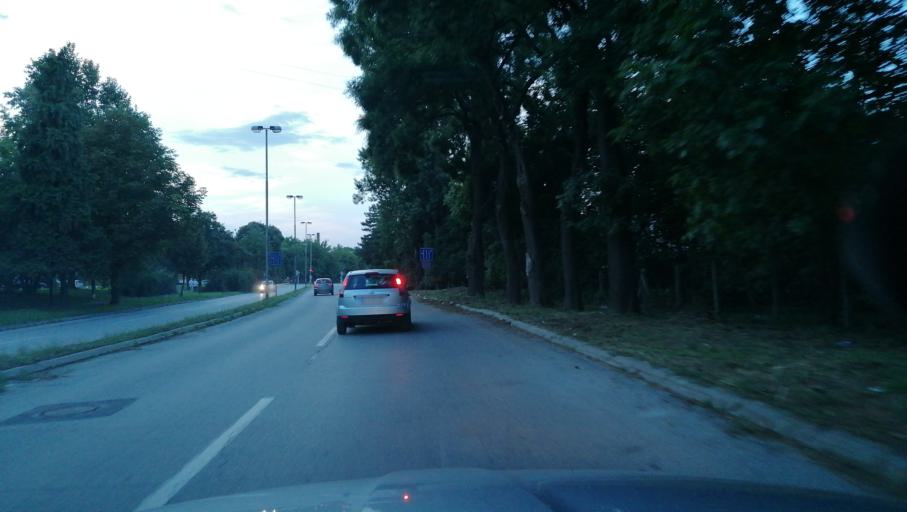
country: RS
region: Central Serbia
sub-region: Kolubarski Okrug
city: Valjevo
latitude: 44.2734
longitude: 19.9087
